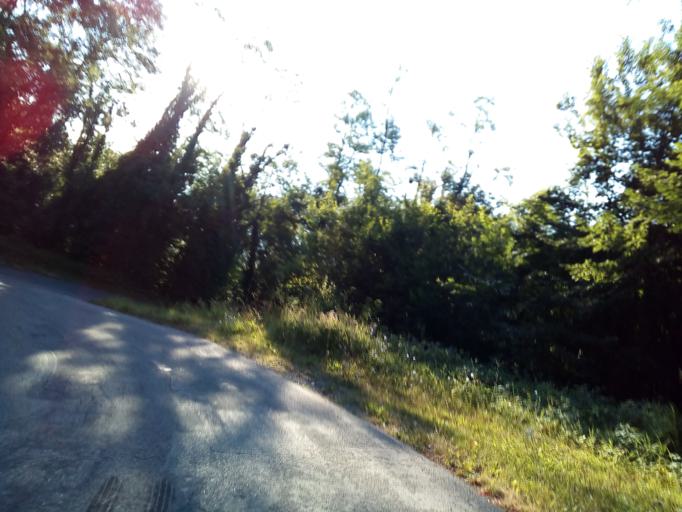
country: FR
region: Rhone-Alpes
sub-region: Departement de l'Isere
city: Barraux
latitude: 45.4211
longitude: 5.9829
